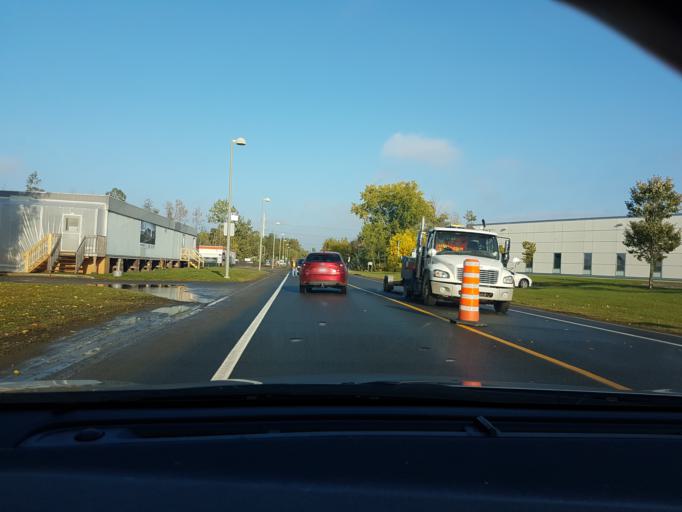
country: CA
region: Quebec
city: L'Ancienne-Lorette
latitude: 46.7974
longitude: -71.3024
